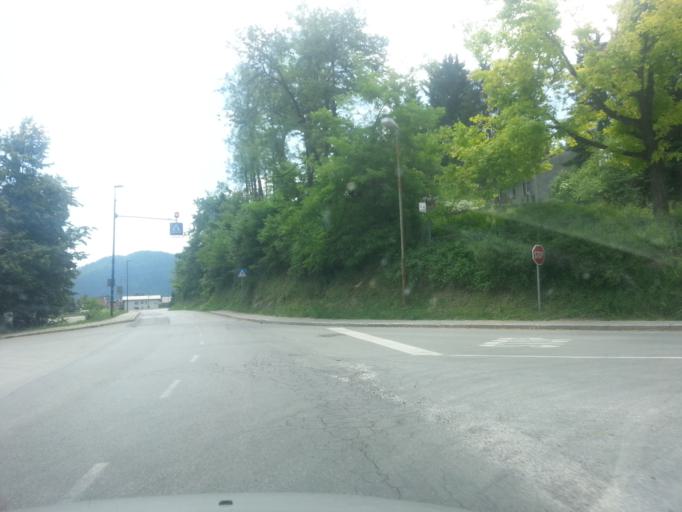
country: SI
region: Vrhnika
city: Vrhnika
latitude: 45.9743
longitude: 14.2914
